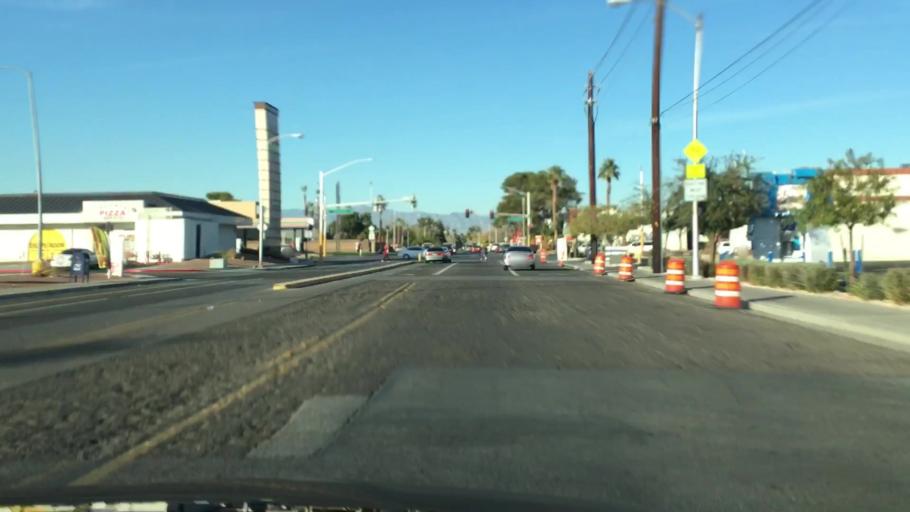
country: US
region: Nevada
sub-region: Clark County
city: Paradise
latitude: 36.1000
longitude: -115.1279
